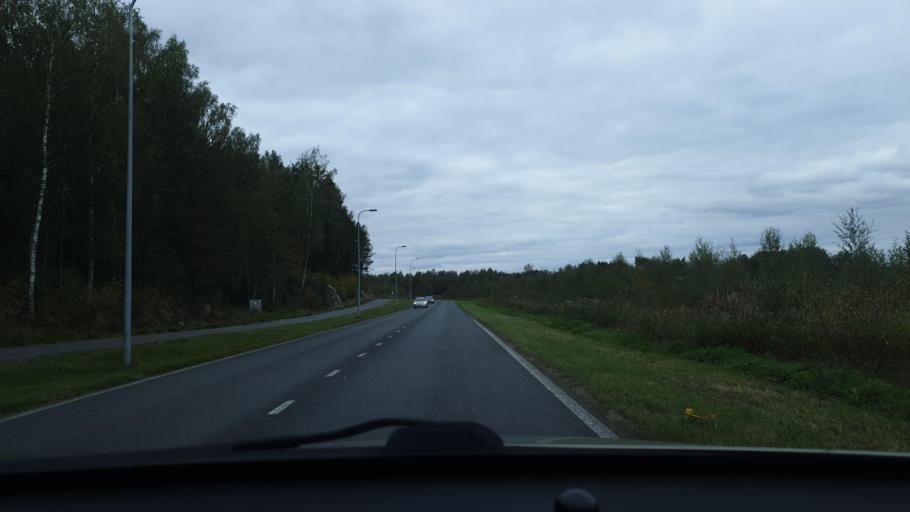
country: FI
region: Ostrobothnia
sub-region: Vaasa
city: Teeriniemi
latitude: 63.0983
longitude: 21.6978
